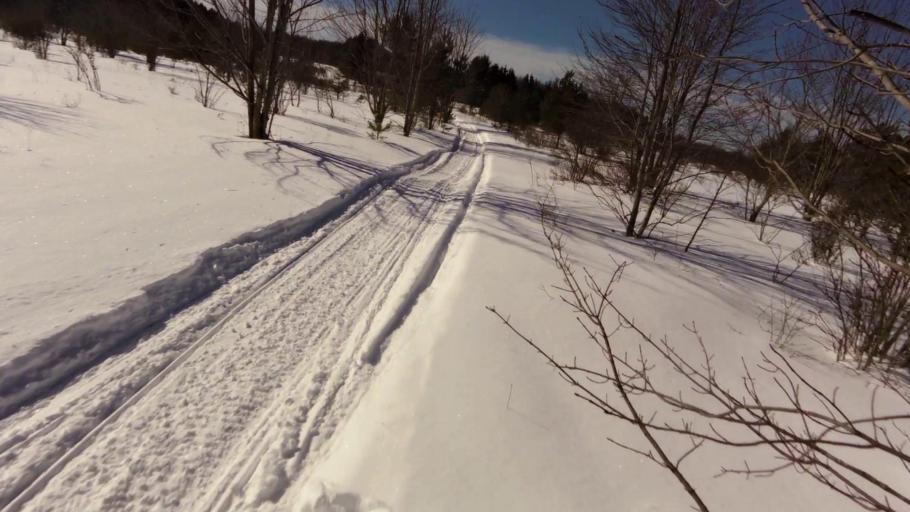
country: US
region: New York
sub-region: Cattaraugus County
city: Franklinville
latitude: 42.3449
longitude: -78.3766
